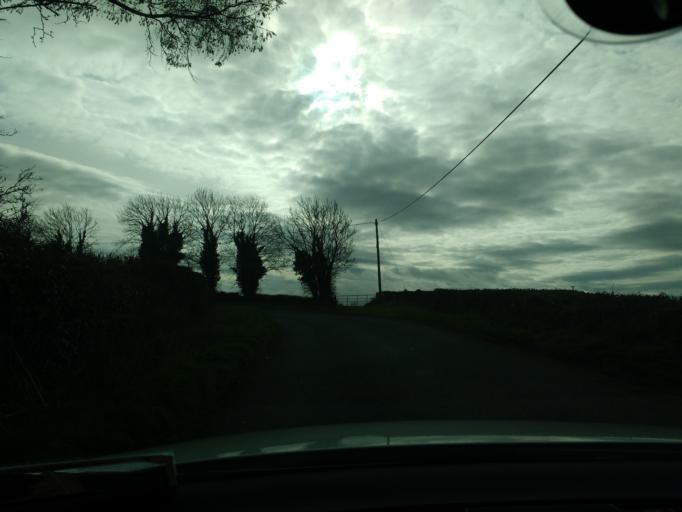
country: IE
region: Leinster
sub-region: Laois
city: Rathdowney
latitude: 52.6865
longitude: -7.6174
